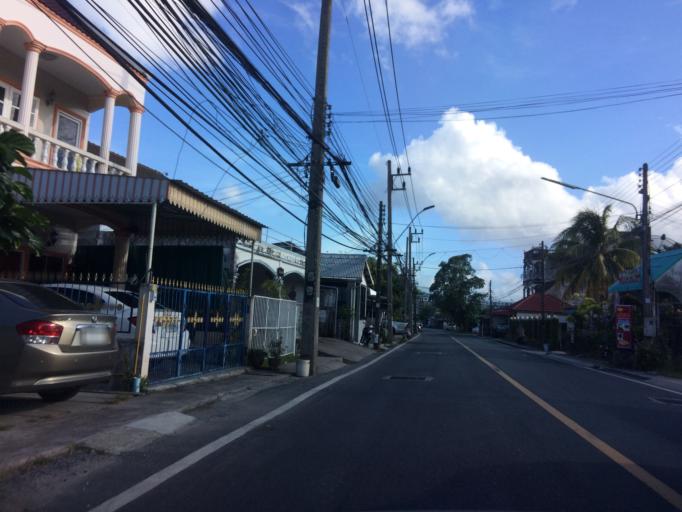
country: TH
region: Phuket
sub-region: Amphoe Kathu
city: Kathu
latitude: 7.9149
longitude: 98.3469
